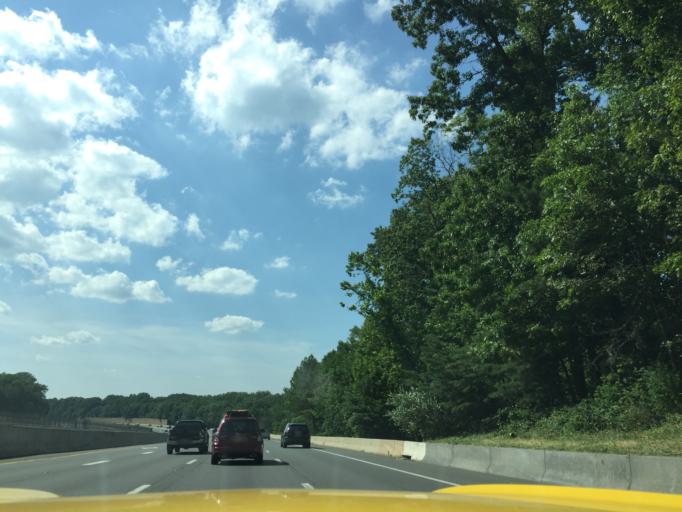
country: US
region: Virginia
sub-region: Fairfax County
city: Wolf Trap
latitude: 38.9378
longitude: -77.2684
